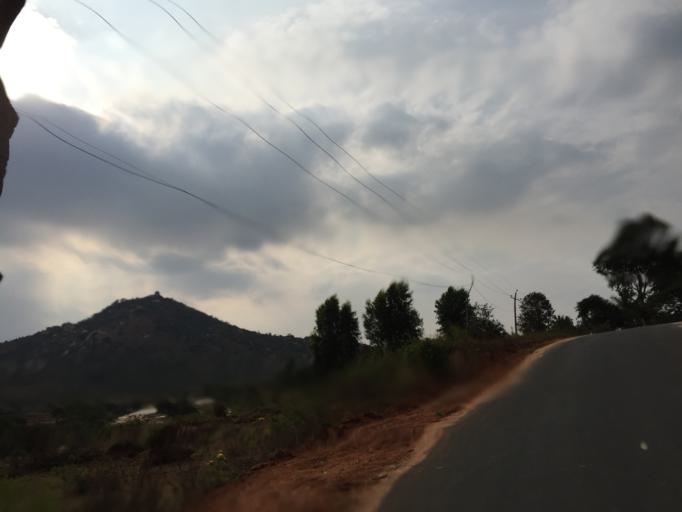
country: IN
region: Karnataka
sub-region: Chikkaballapur
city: Chik Ballapur
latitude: 13.5530
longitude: 77.7457
